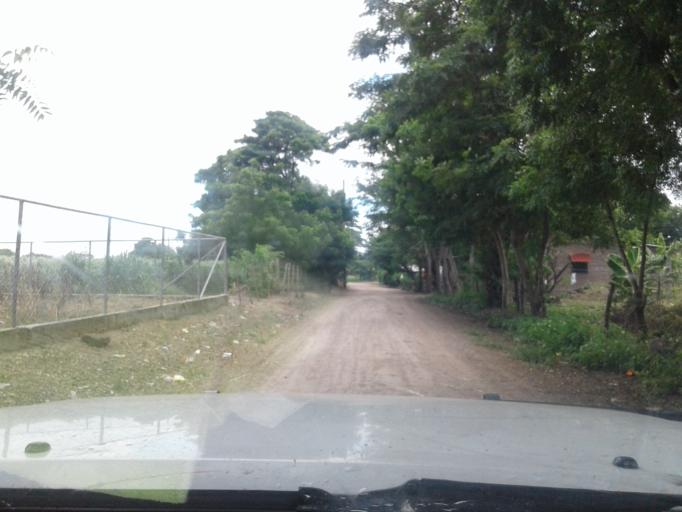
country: NI
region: Matagalpa
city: Ciudad Dario
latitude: 12.8433
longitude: -86.1227
